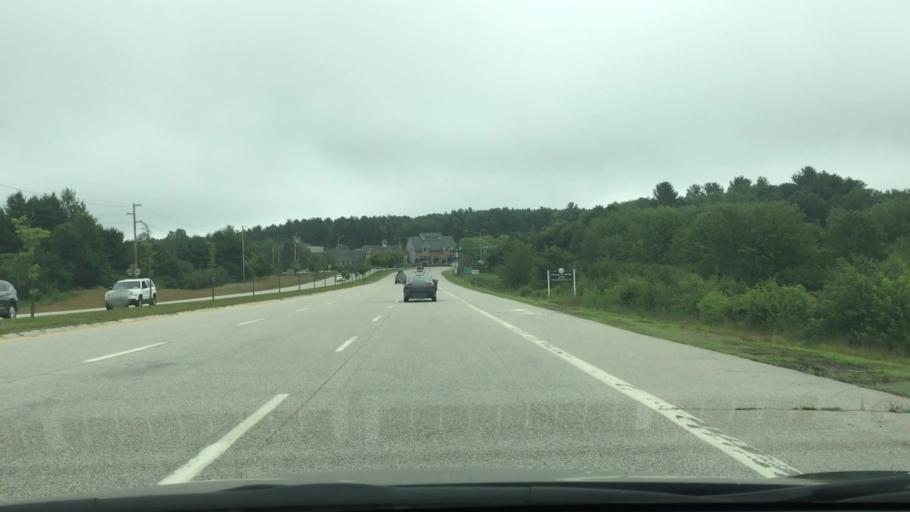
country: US
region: Maine
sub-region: York County
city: York Harbor
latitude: 43.1556
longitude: -70.6626
